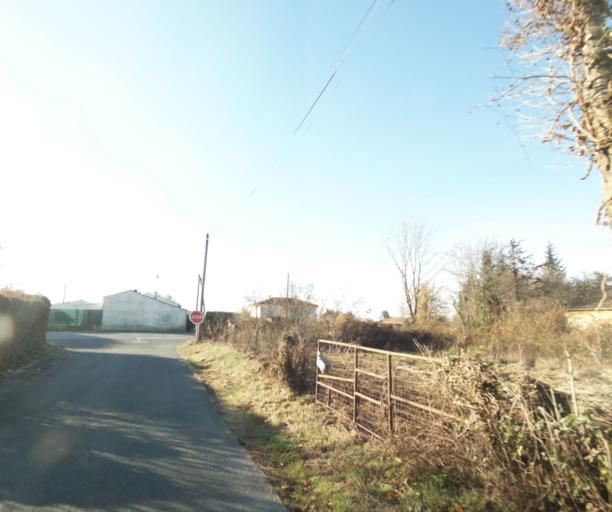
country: FR
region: Poitou-Charentes
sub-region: Departement de la Charente-Maritime
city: Fontcouverte
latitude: 45.7457
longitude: -0.5866
